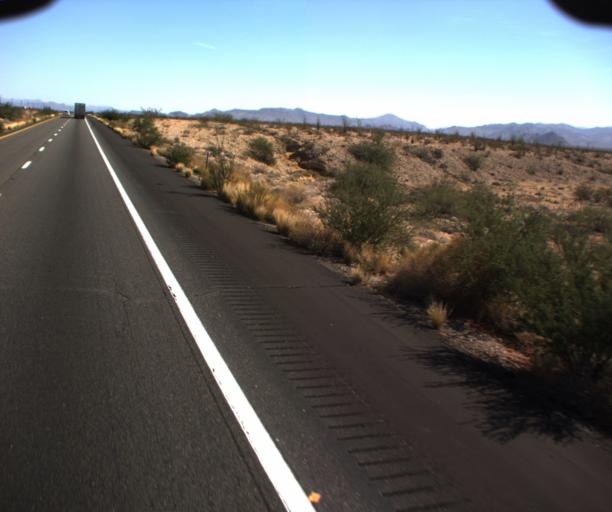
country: US
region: Arizona
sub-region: Mohave County
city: Kingman
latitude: 34.9840
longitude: -114.1393
